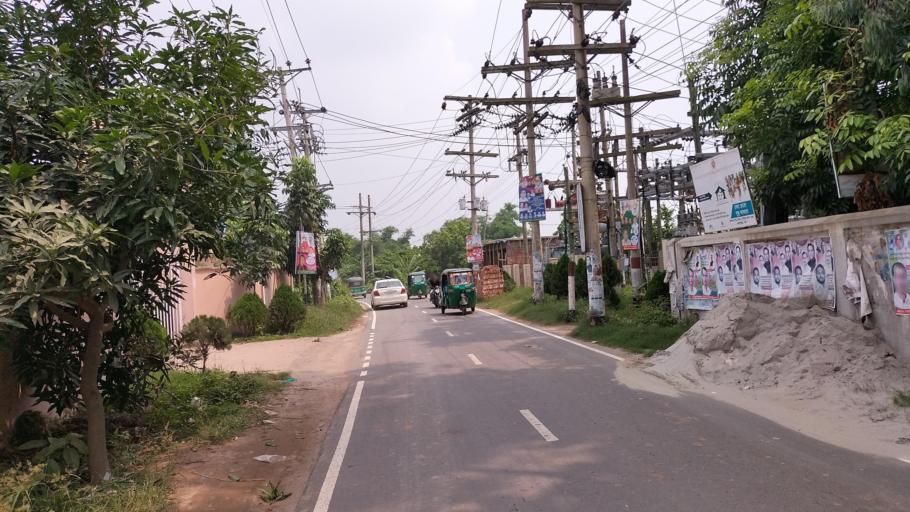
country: BD
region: Dhaka
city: Azimpur
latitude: 23.7228
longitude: 90.2740
